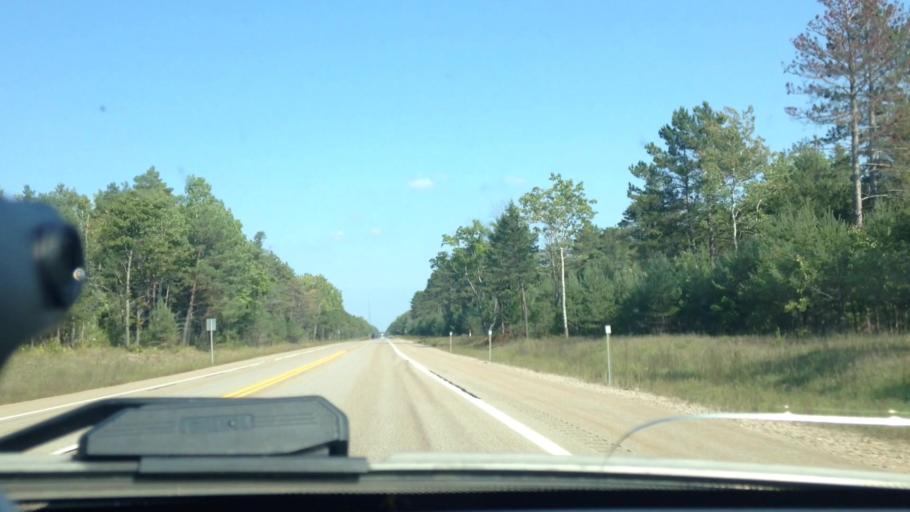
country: US
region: Michigan
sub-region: Chippewa County
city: Sault Ste. Marie
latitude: 46.3660
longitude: -84.7564
